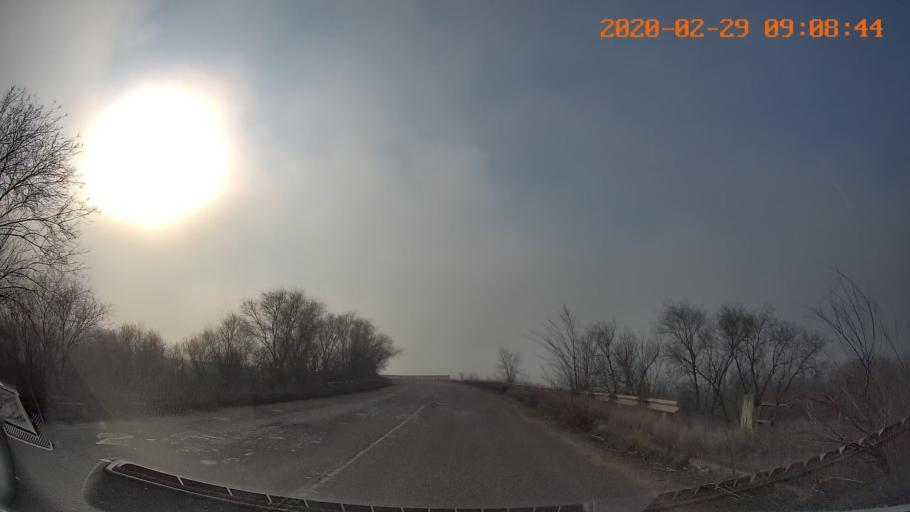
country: MD
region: Telenesti
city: Tiraspolul Nou
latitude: 46.8471
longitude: 29.7536
